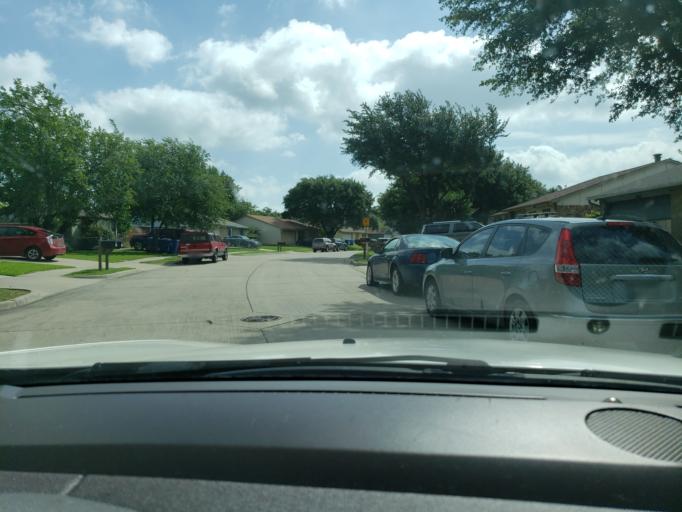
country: US
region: Texas
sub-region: Dallas County
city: Rowlett
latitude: 32.9111
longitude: -96.5730
